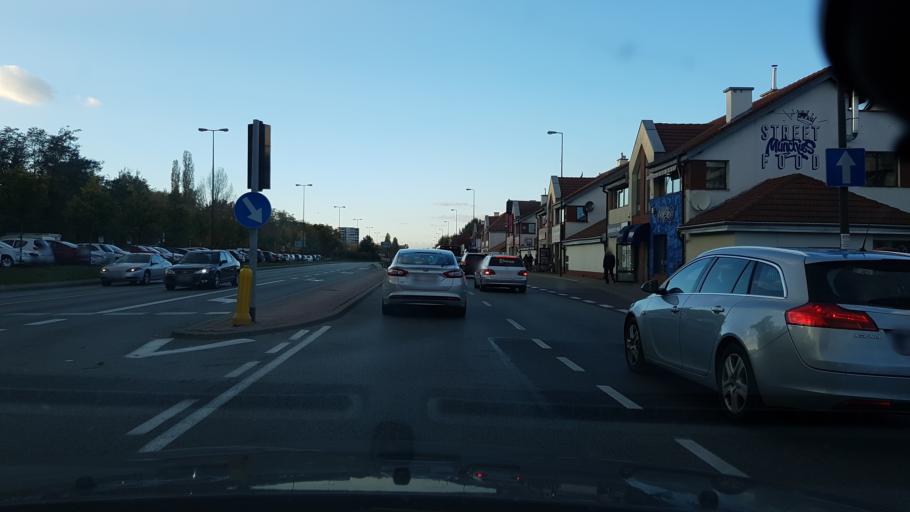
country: PL
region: Masovian Voivodeship
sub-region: Warszawa
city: Ursynow
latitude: 52.1454
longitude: 21.0635
